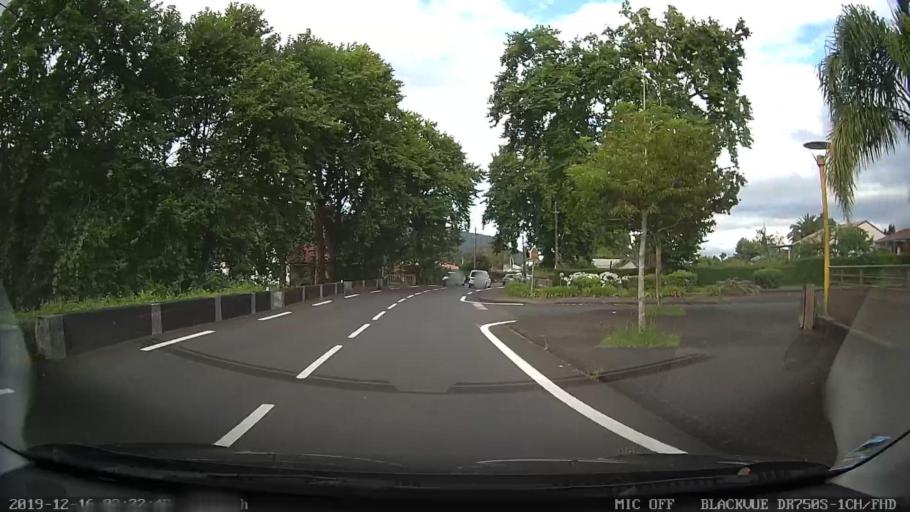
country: RE
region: Reunion
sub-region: Reunion
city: Salazie
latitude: -21.1461
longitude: 55.6180
